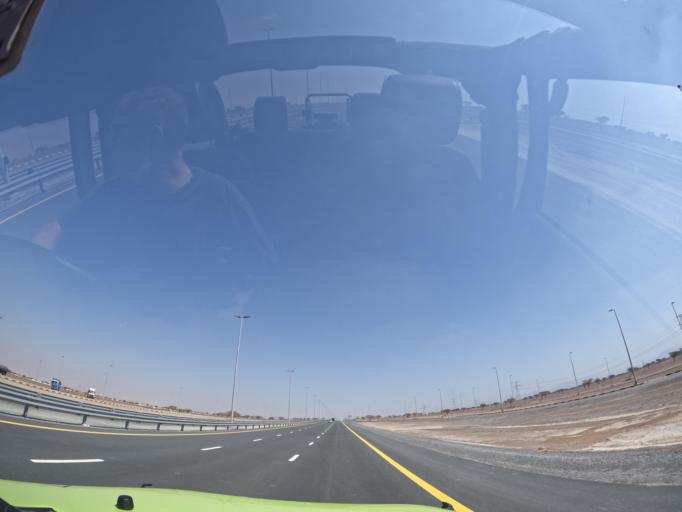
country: AE
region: Ash Shariqah
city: Adh Dhayd
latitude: 24.9551
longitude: 55.8375
